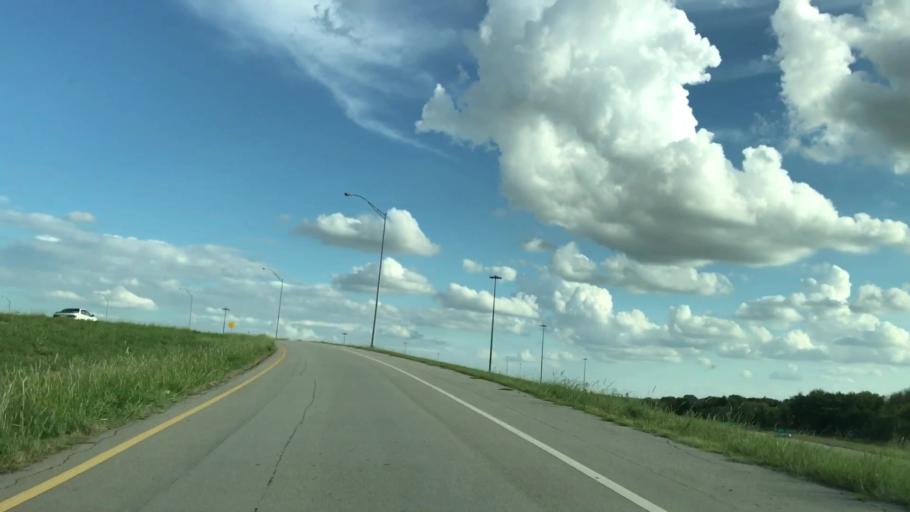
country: US
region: Texas
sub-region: Dallas County
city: Coppell
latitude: 32.9523
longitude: -97.0417
